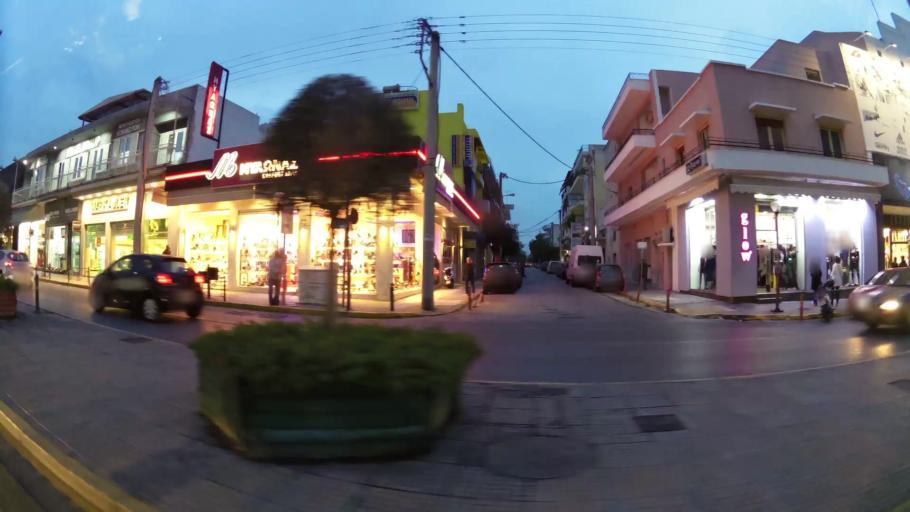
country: GR
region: Attica
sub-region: Nomarchia Athinas
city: Aigaleo
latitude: 37.9912
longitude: 23.6829
